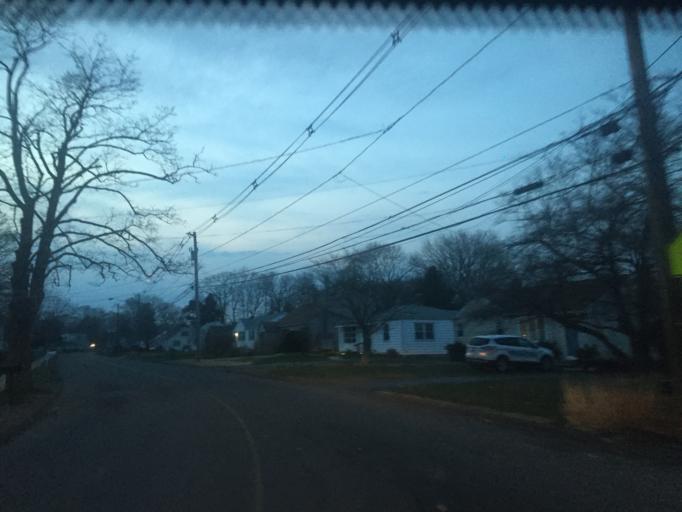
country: US
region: Connecticut
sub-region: New Haven County
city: Branford Center
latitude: 41.2692
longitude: -72.8053
